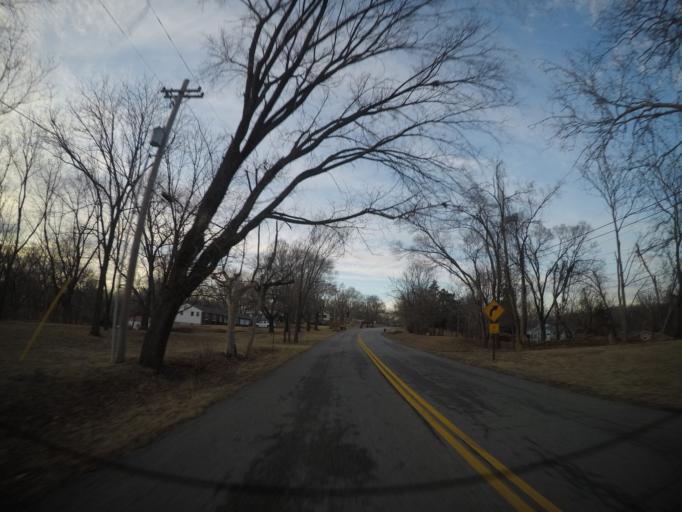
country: US
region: Kansas
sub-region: Johnson County
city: Shawnee
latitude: 39.0764
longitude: -94.7602
